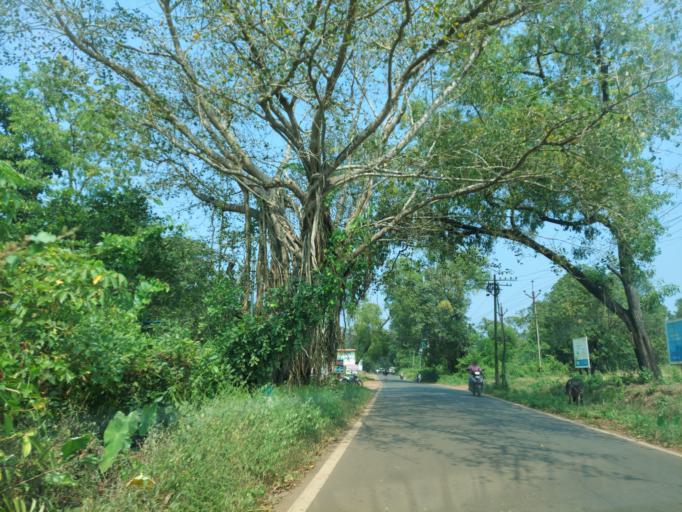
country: IN
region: Maharashtra
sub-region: Sindhudurg
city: Kudal
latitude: 15.9952
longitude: 73.6849
